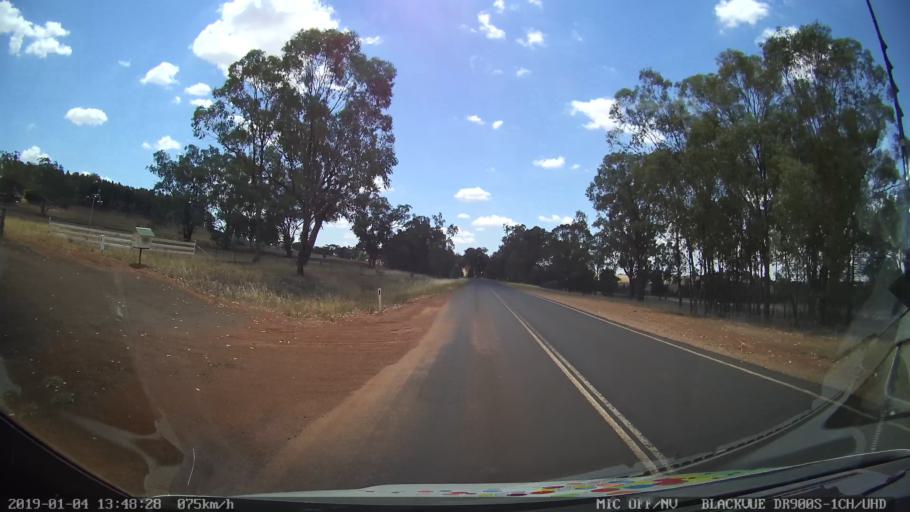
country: AU
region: New South Wales
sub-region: Dubbo Municipality
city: Dubbo
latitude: -32.4422
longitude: 148.5842
